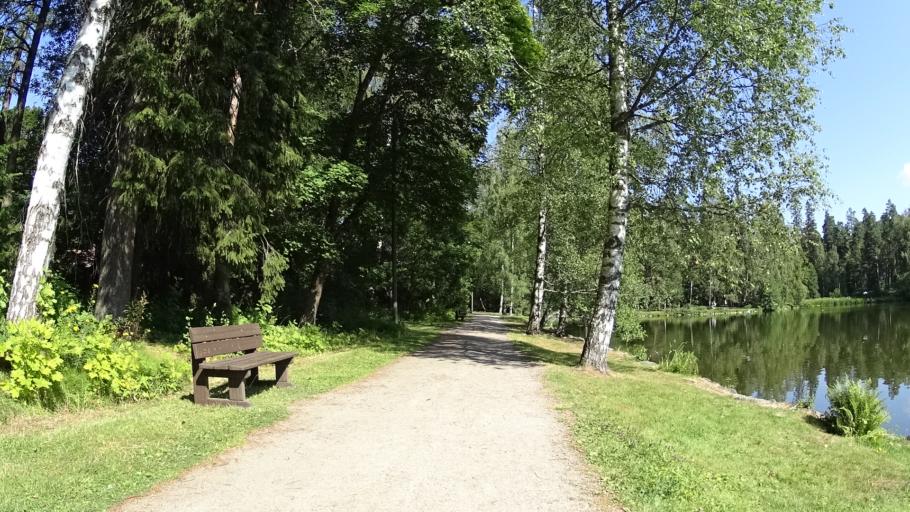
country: FI
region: Haeme
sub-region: Haemeenlinna
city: Haemeenlinna
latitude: 61.0225
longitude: 24.4546
